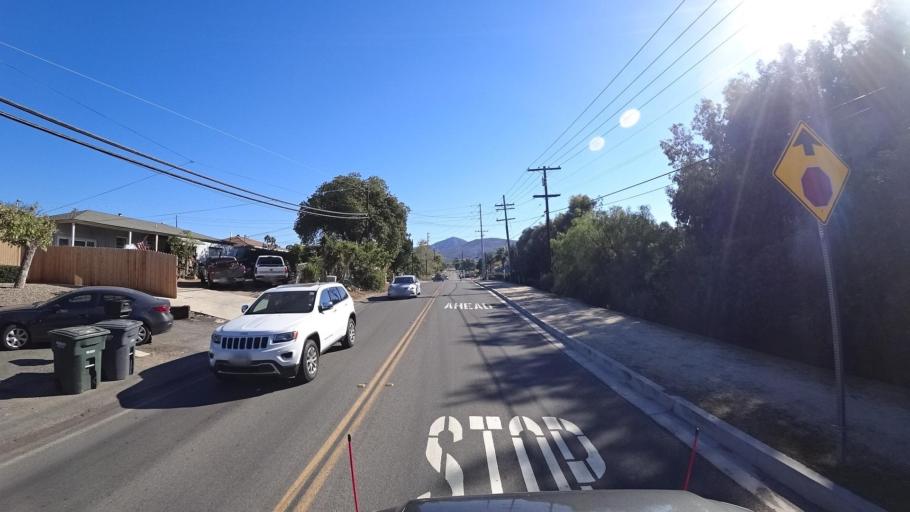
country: US
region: California
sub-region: San Diego County
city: Bonita
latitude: 32.6765
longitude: -117.0088
